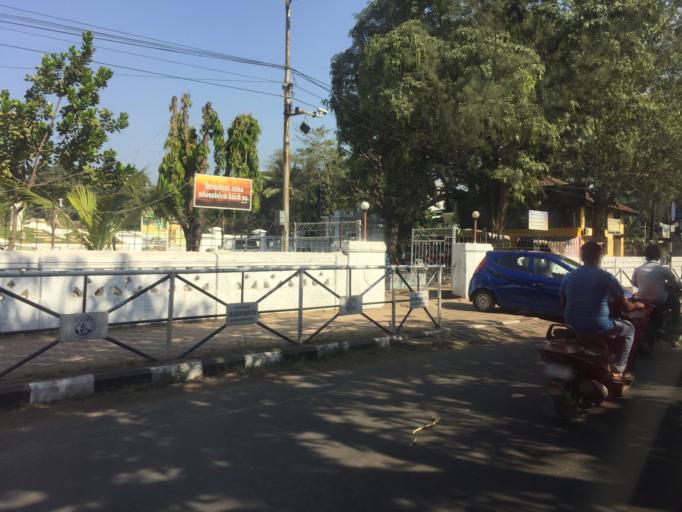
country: IN
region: Goa
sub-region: South Goa
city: Vasco Da Gama
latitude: 15.3993
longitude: 73.8171
